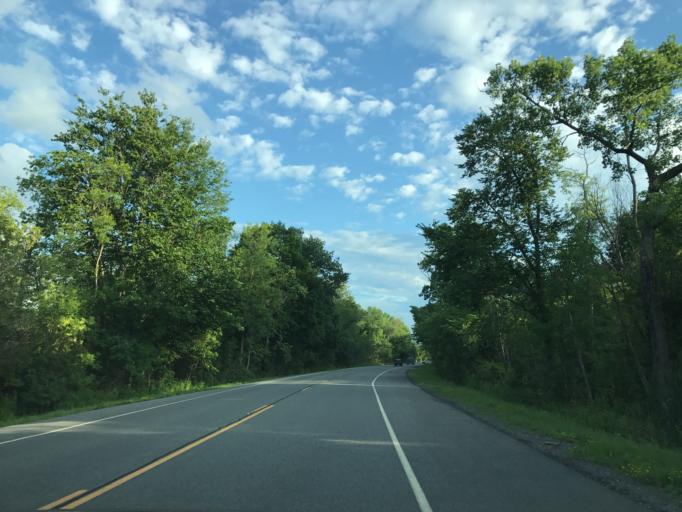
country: US
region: New York
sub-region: Saratoga County
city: Schuylerville
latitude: 43.0311
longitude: -73.5935
